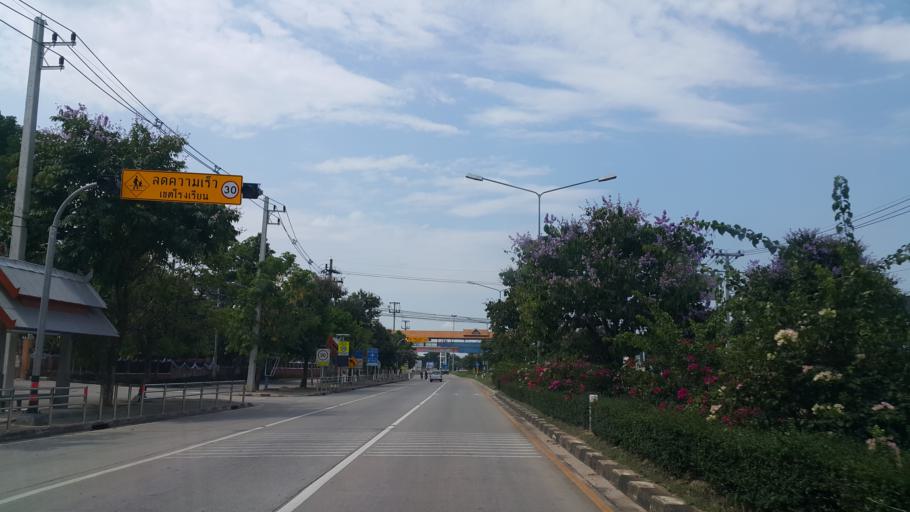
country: TH
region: Chiang Rai
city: Chiang Rai
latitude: 19.9266
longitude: 99.8629
